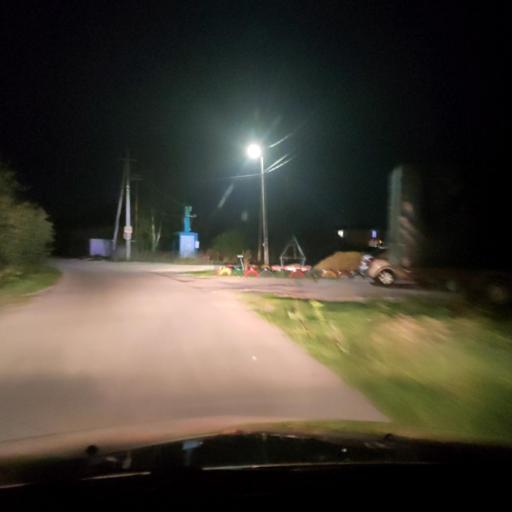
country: RU
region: Voronezj
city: Novaya Usman'
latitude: 51.6357
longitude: 39.3871
